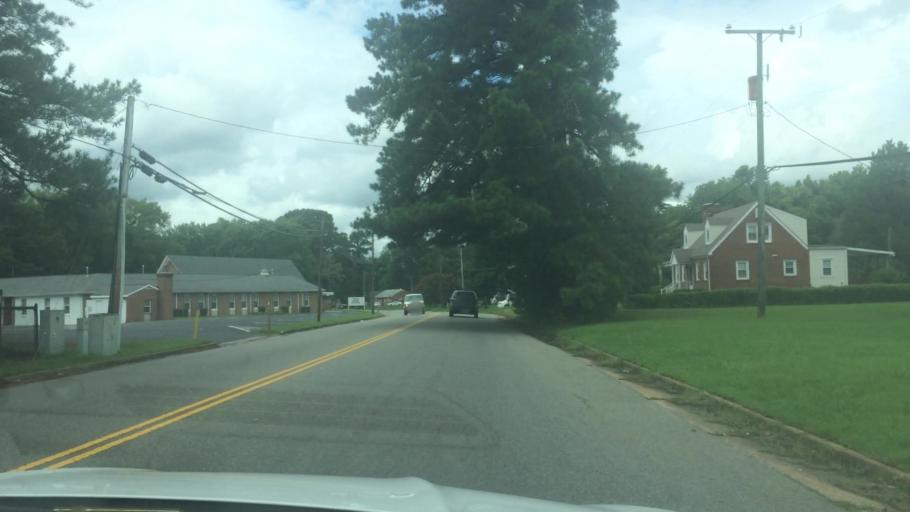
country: US
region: Virginia
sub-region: City of Williamsburg
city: Williamsburg
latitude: 37.2644
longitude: -76.6662
